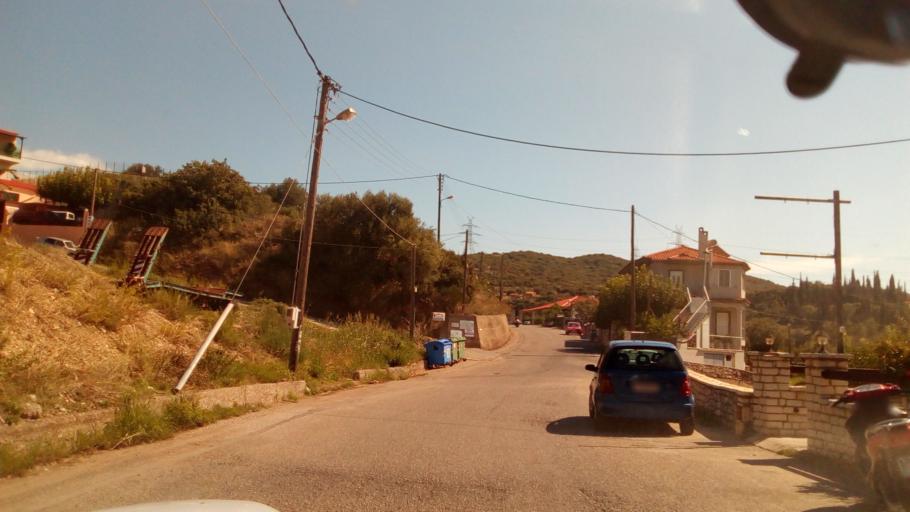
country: GR
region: West Greece
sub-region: Nomos Aitolias kai Akarnanias
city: Nafpaktos
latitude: 38.4163
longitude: 21.8988
